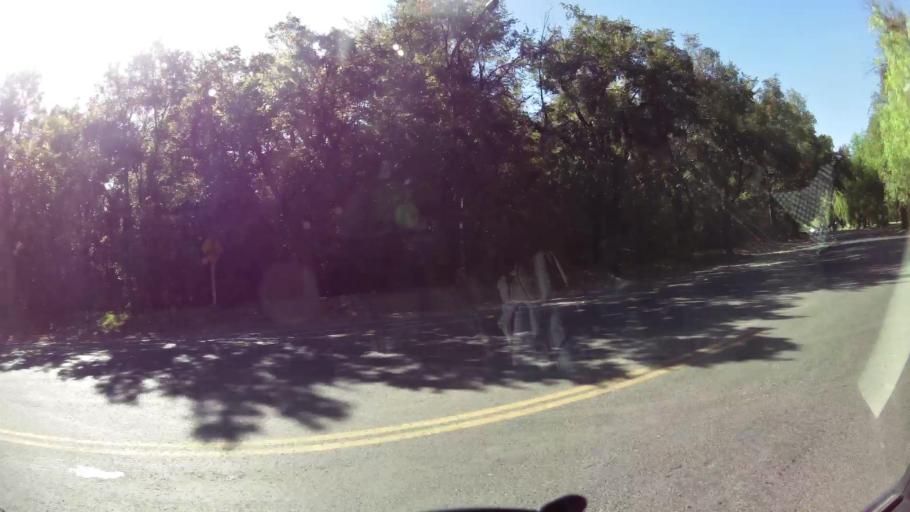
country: AR
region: Mendoza
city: Mendoza
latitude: -32.8914
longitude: -68.8733
